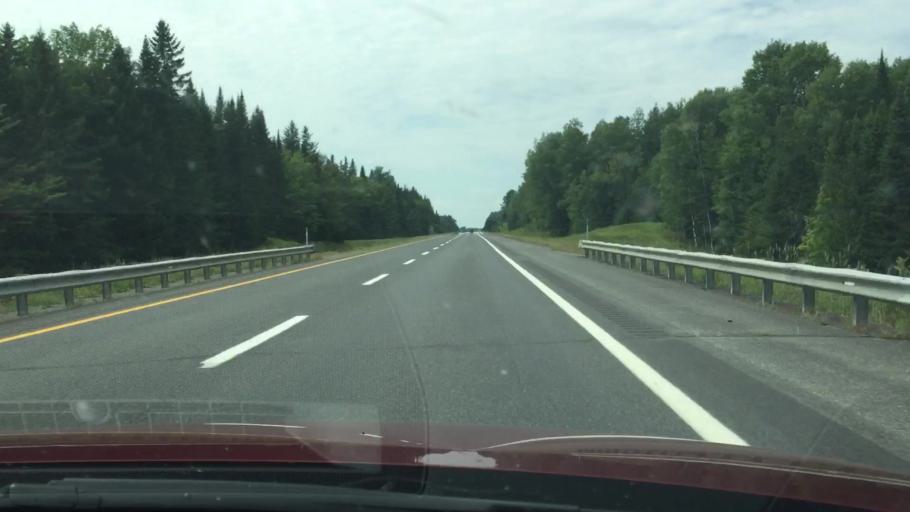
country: US
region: Maine
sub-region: Aroostook County
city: Houlton
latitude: 46.1410
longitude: -67.9871
